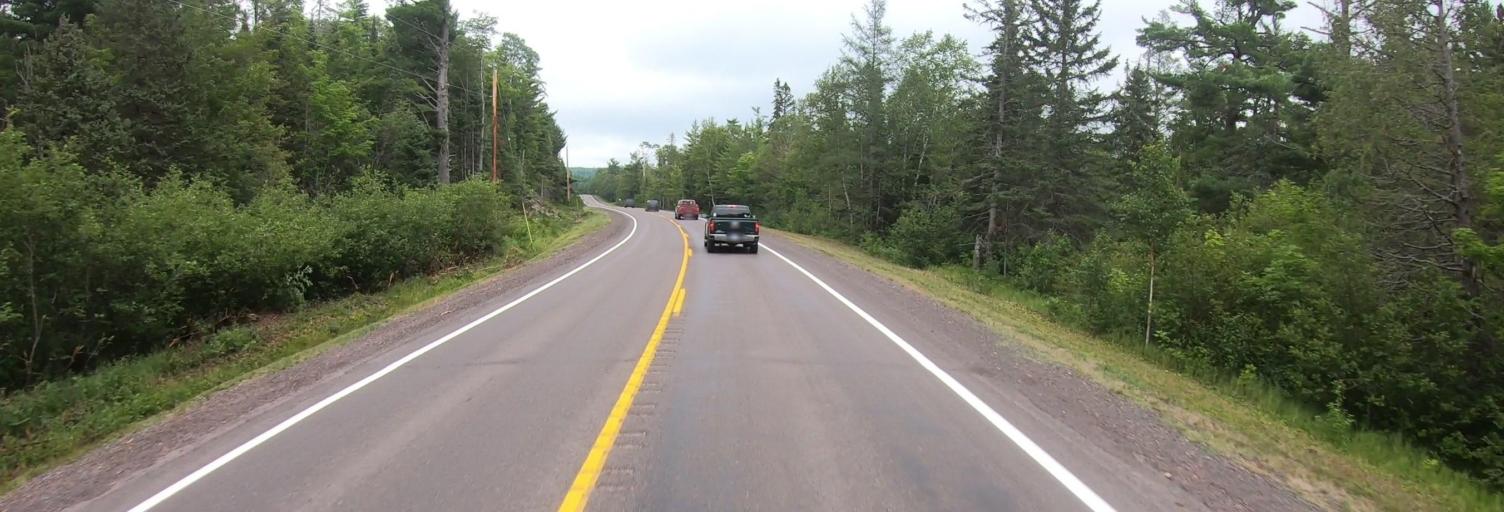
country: US
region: Michigan
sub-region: Keweenaw County
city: Eagle River
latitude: 47.4111
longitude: -88.1689
